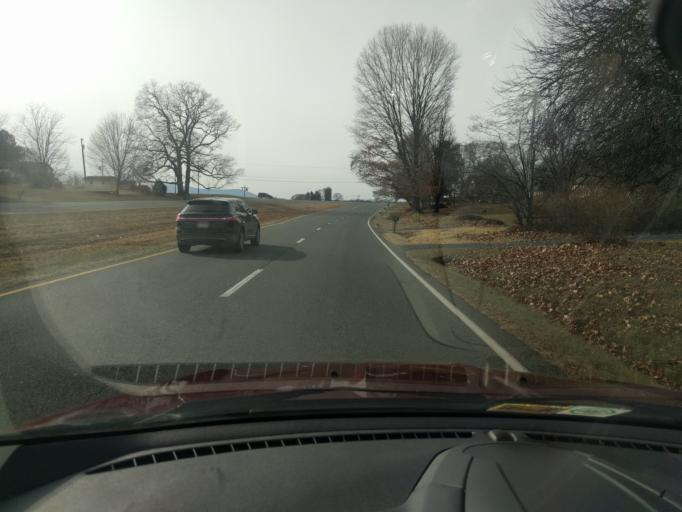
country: US
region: Virginia
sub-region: Augusta County
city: Lyndhurst
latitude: 38.0485
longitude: -78.9726
